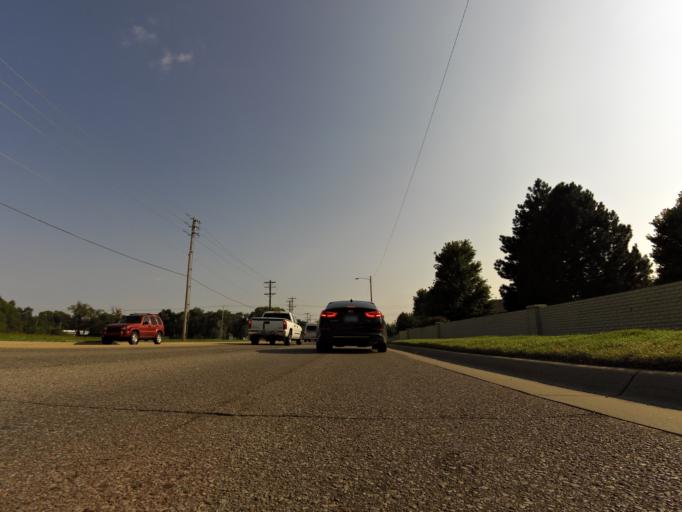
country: US
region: Kansas
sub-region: Sedgwick County
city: Maize
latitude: 37.7391
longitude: -97.4263
